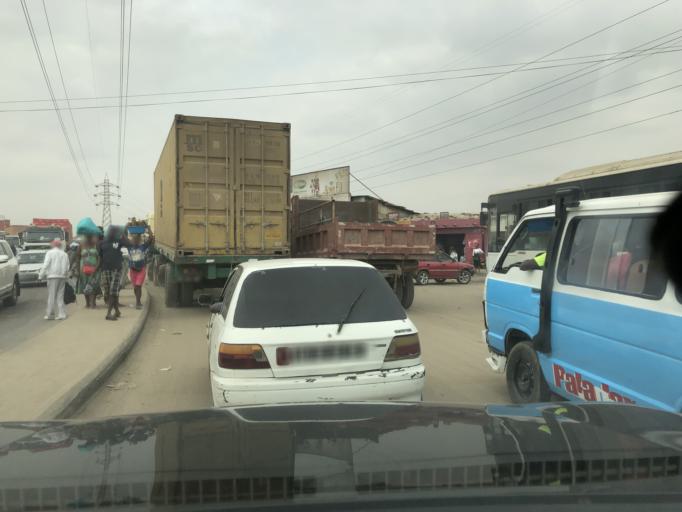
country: AO
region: Luanda
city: Luanda
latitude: -8.8165
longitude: 13.2781
